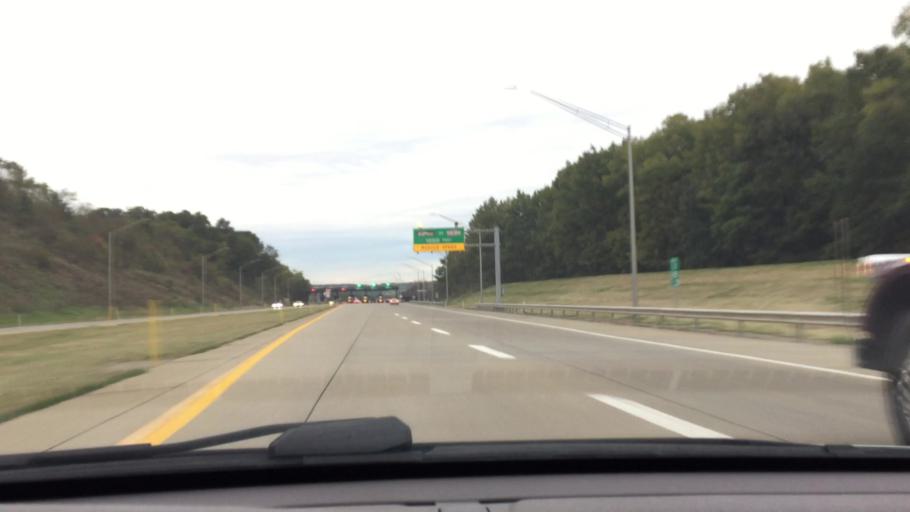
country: US
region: Pennsylvania
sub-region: Lawrence County
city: Oakland
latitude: 40.9419
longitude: -80.3914
